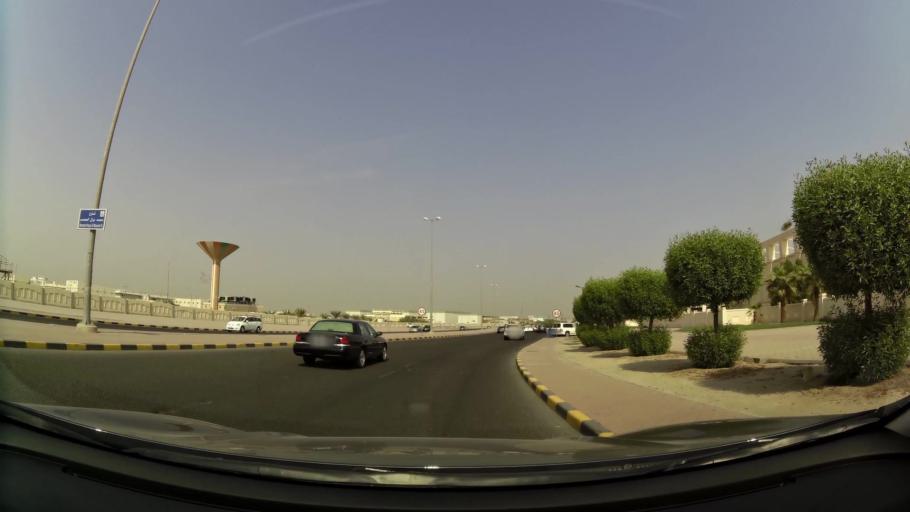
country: KW
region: Al Asimah
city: Ar Rabiyah
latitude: 29.2752
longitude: 47.9158
